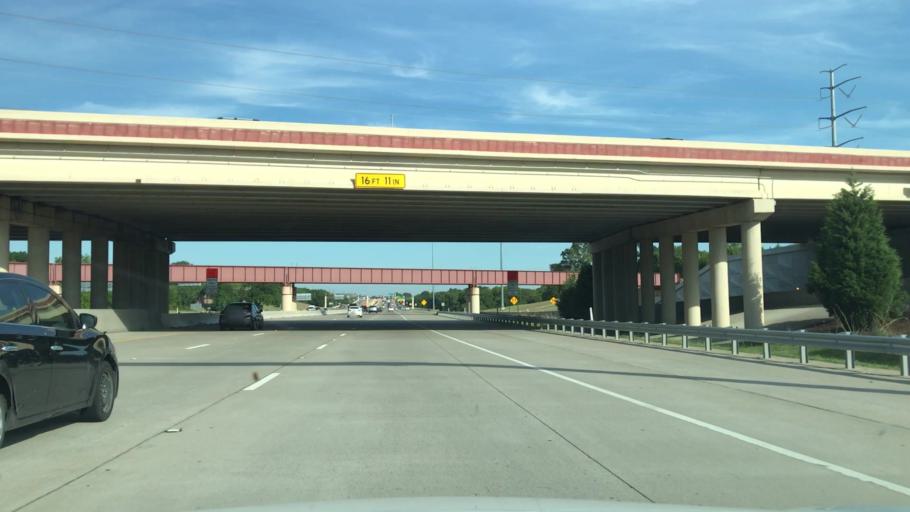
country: US
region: Texas
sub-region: Dallas County
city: Sachse
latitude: 32.9503
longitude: -96.6184
